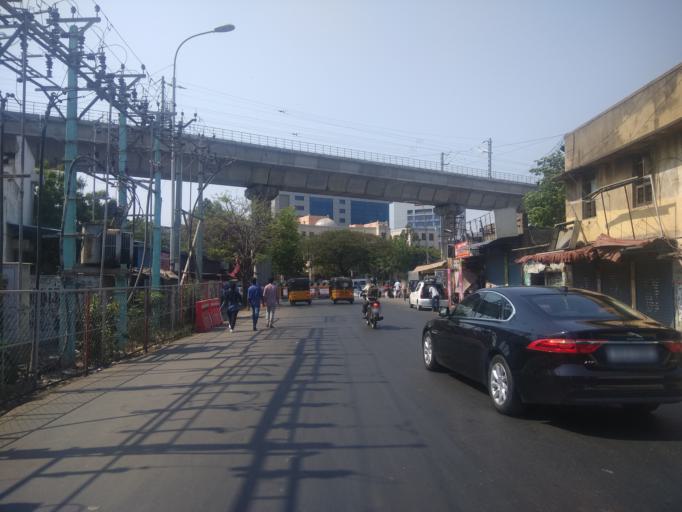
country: IN
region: Tamil Nadu
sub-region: Kancheepuram
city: Alandur
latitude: 13.0077
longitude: 80.2099
